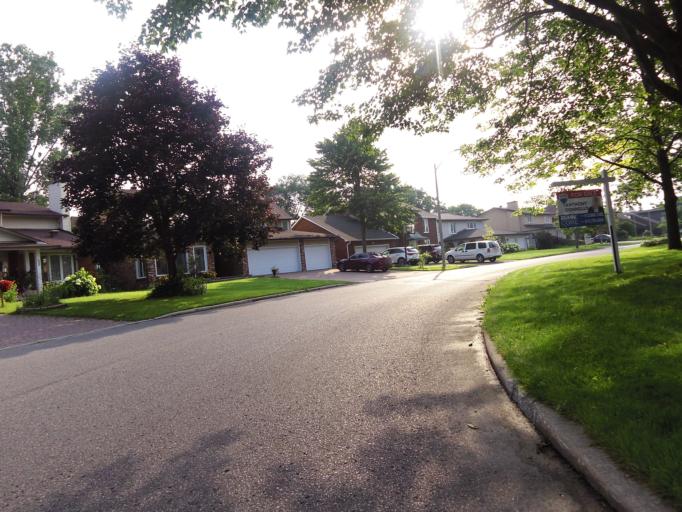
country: CA
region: Ontario
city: Ottawa
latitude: 45.3459
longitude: -75.6696
